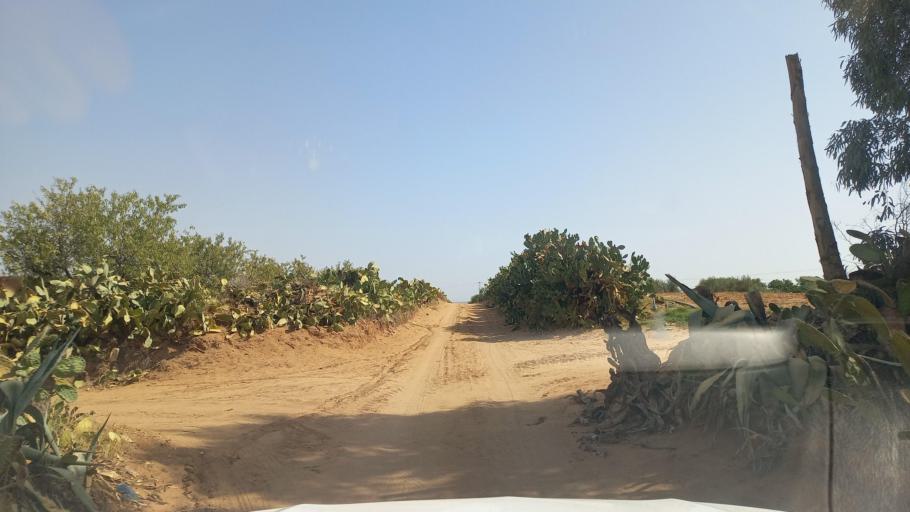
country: TN
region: Al Qasrayn
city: Kasserine
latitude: 35.2336
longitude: 9.0531
